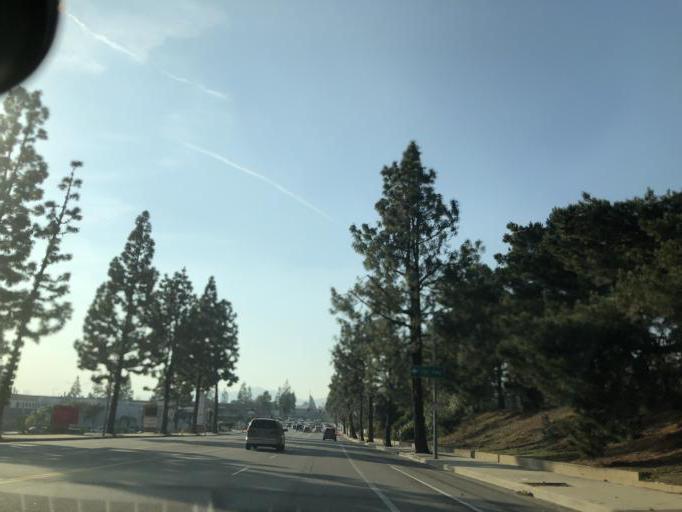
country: US
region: California
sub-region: Los Angeles County
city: Northridge
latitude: 34.2751
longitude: -118.5543
